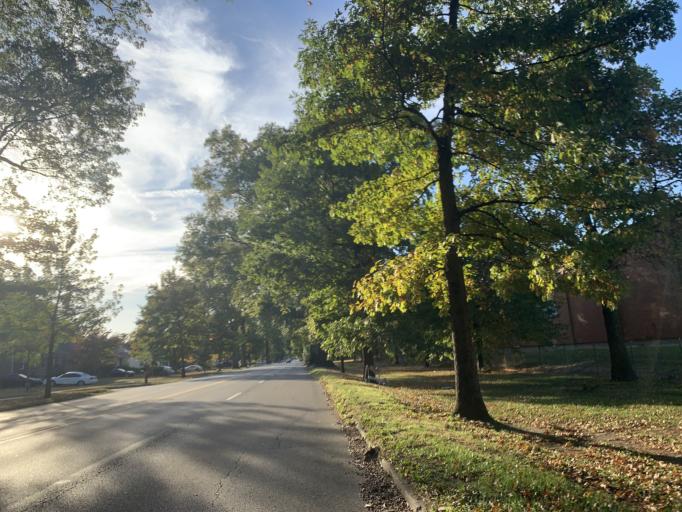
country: US
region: Kentucky
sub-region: Jefferson County
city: Louisville
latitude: 38.2227
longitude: -85.7852
